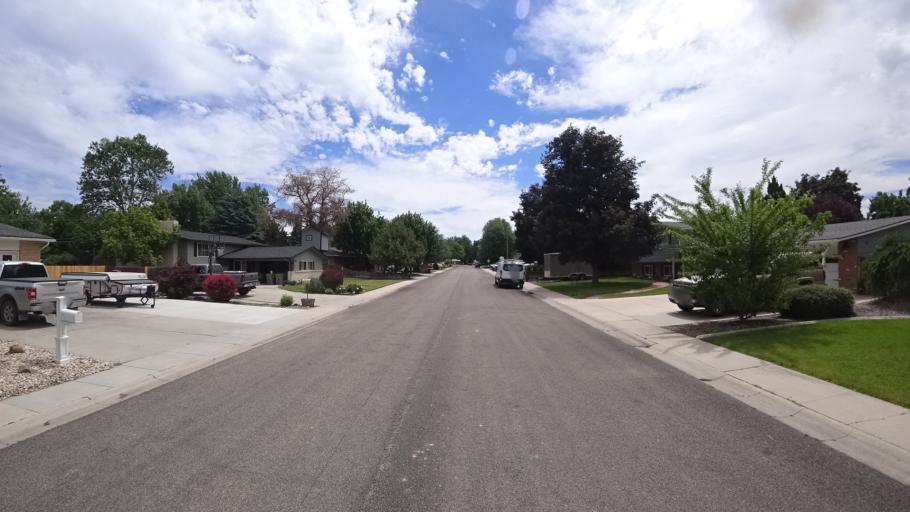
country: US
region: Idaho
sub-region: Ada County
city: Garden City
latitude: 43.6427
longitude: -116.2771
